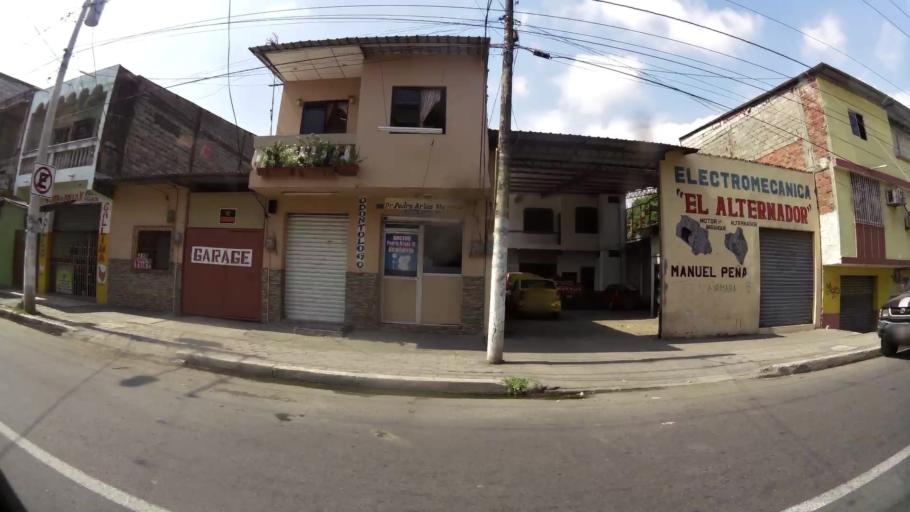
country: EC
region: Guayas
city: Eloy Alfaro
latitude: -2.1592
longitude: -79.8398
